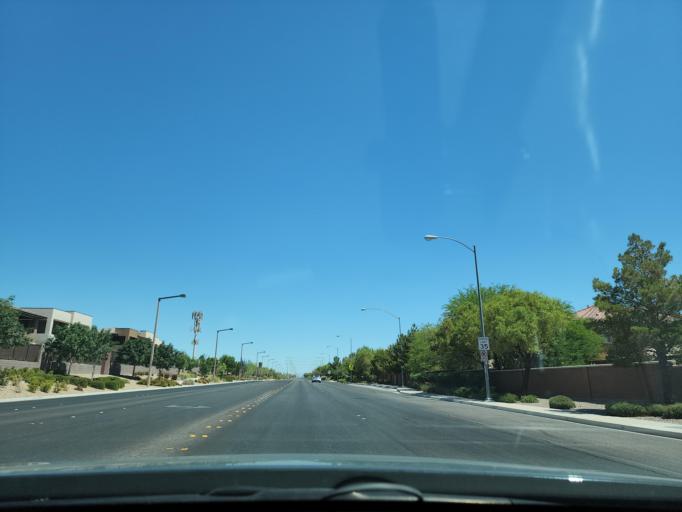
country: US
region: Nevada
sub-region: Clark County
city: Summerlin South
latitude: 36.0777
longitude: -115.3156
